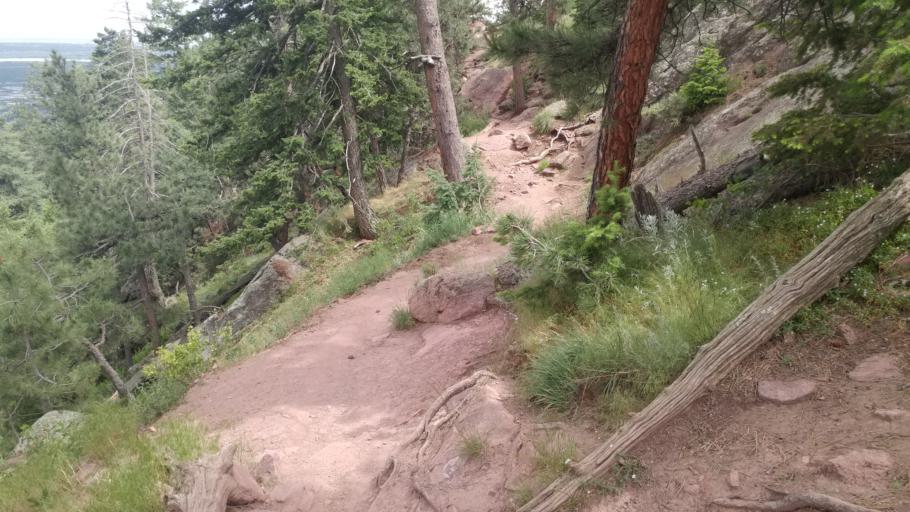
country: US
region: Colorado
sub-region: Boulder County
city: Boulder
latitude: 40.0351
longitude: -105.3044
